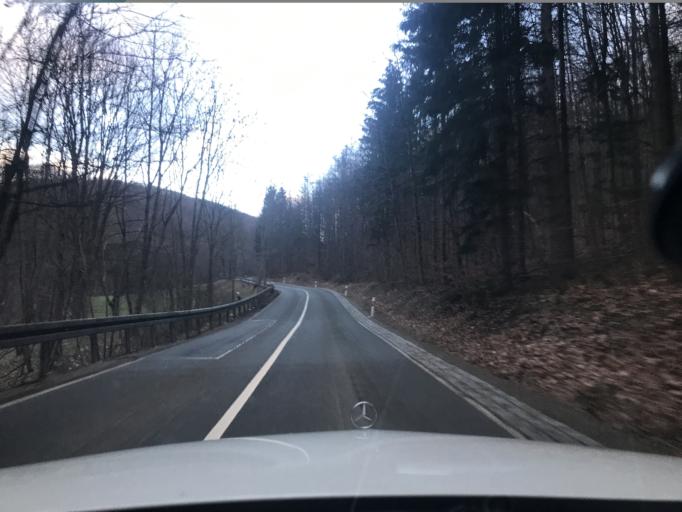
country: DE
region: Thuringia
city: Effelder
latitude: 51.2143
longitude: 10.2734
